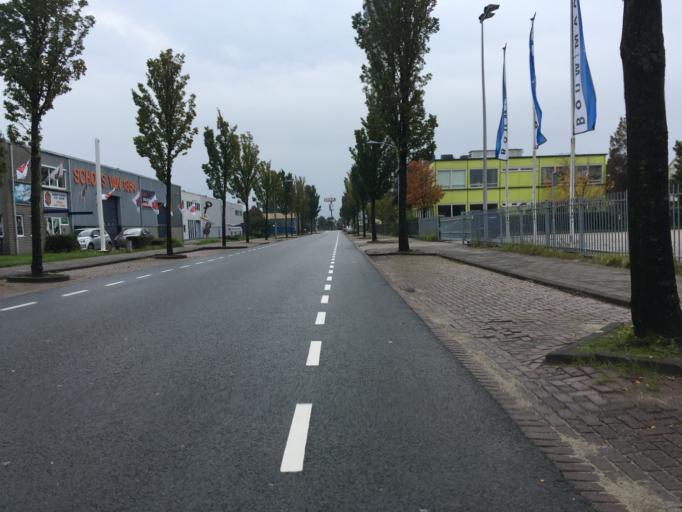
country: NL
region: North Holland
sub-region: Gemeente Haarlem
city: Haarlem
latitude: 52.3905
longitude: 4.6685
